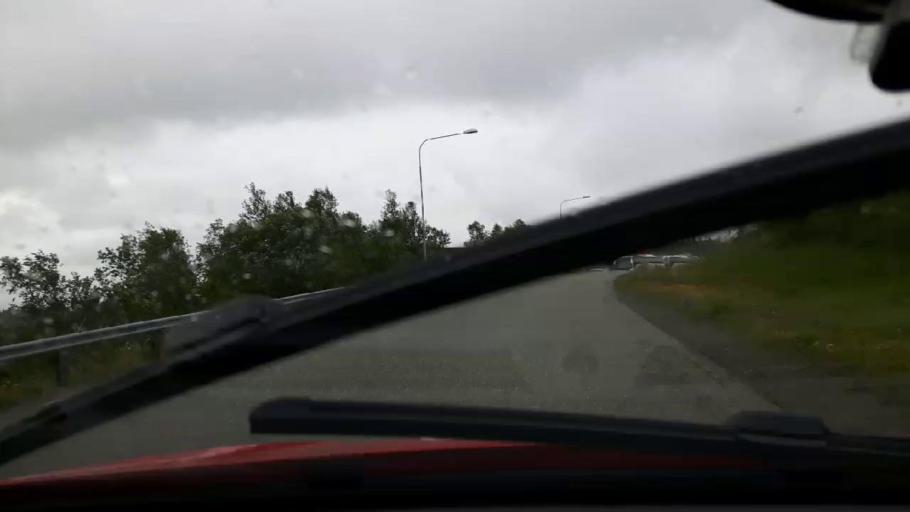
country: NO
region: Nord-Trondelag
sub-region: Meraker
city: Meraker
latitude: 63.3106
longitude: 12.1105
